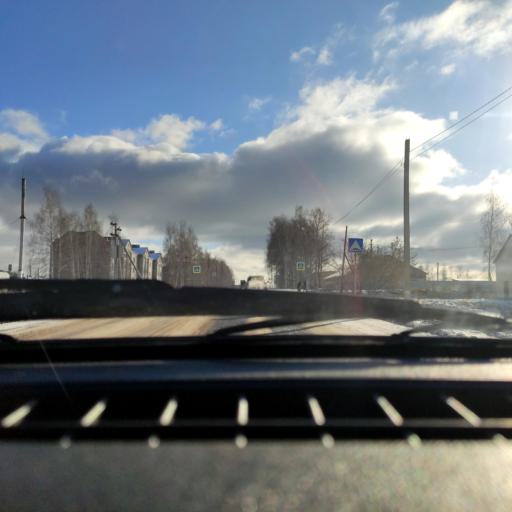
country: RU
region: Bashkortostan
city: Iglino
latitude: 54.8185
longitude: 56.4022
